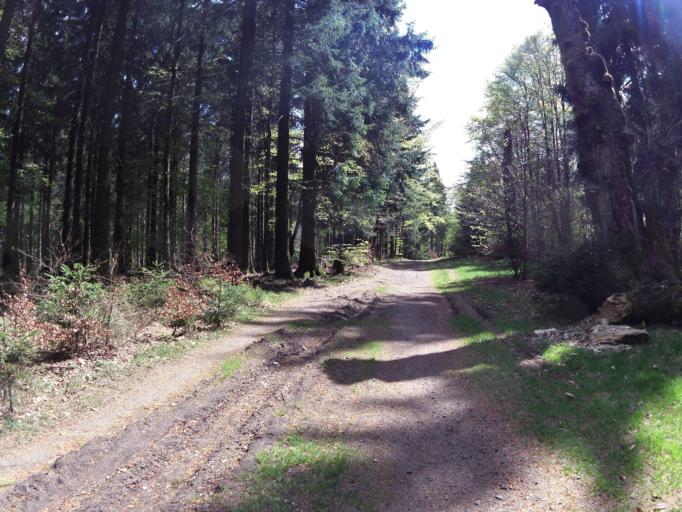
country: DE
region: Thuringia
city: Friedrichroda
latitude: 50.8208
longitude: 10.5401
